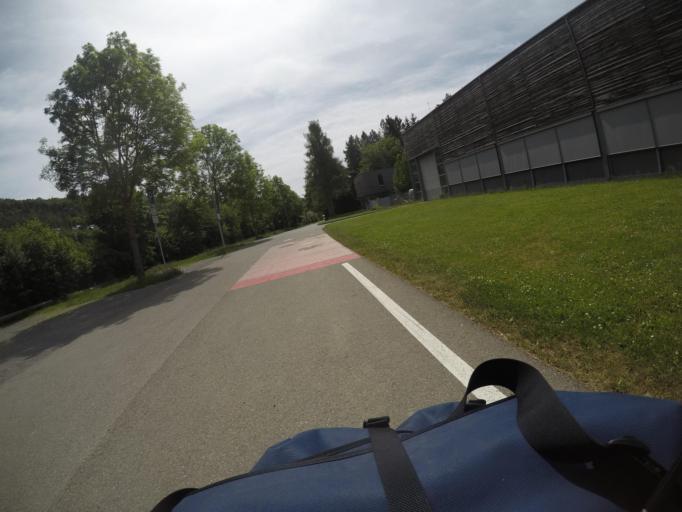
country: DE
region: Baden-Wuerttemberg
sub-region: Karlsruhe Region
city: Nagold
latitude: 48.5642
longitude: 8.7220
